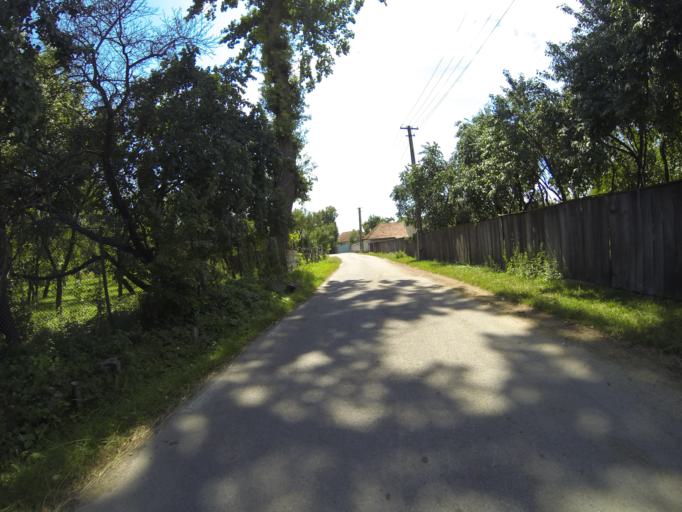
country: RO
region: Brasov
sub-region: Comuna Sinca Veche
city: Sinca Veche
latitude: 45.7622
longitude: 25.1658
